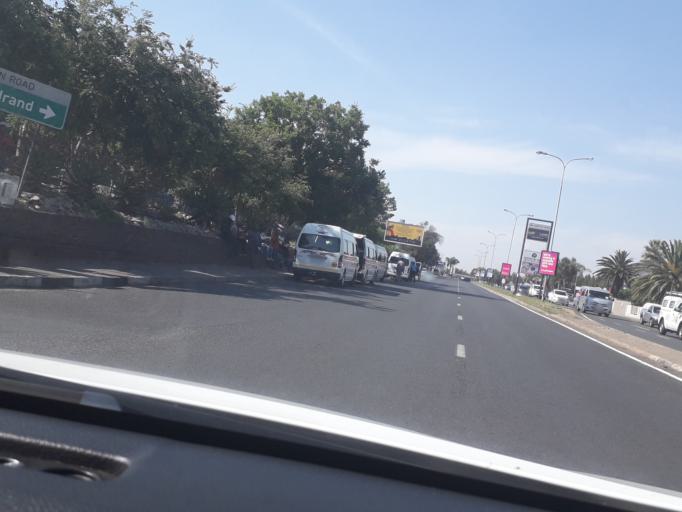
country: ZA
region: Gauteng
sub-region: City of Johannesburg Metropolitan Municipality
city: Johannesburg
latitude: -26.0775
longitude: 28.0111
